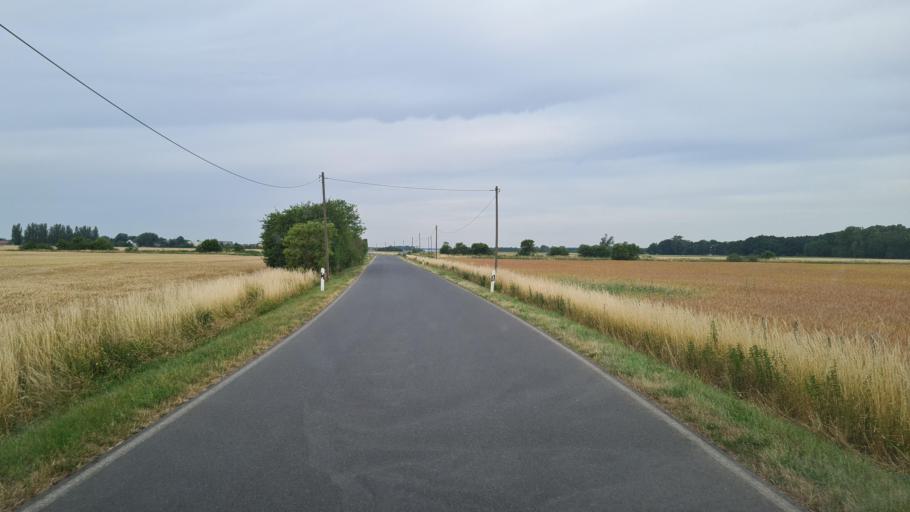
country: DE
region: Saxony-Anhalt
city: Jessen
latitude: 51.7562
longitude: 12.9676
